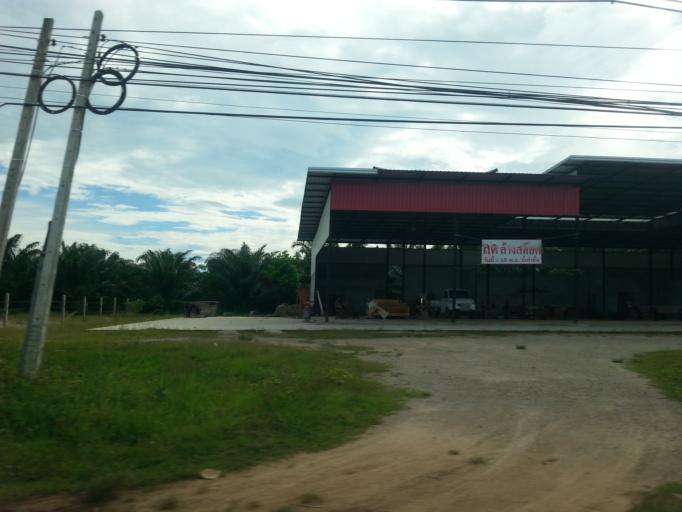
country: TH
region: Krabi
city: Nuea Khlong
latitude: 8.0571
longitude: 99.0197
